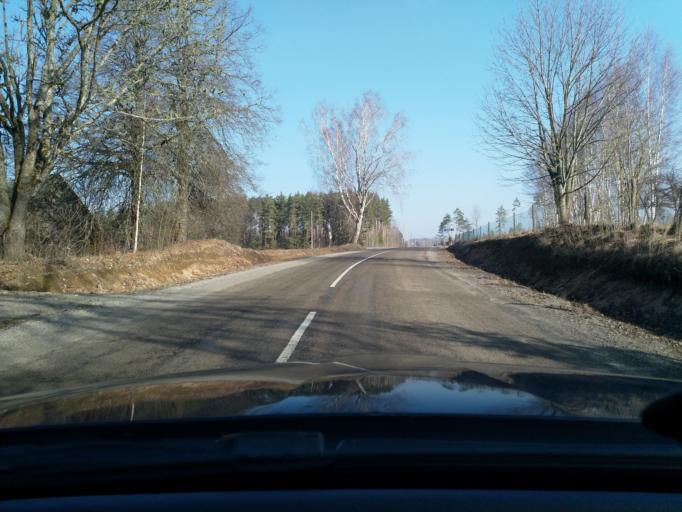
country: LV
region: Kuldigas Rajons
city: Kuldiga
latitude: 56.8700
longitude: 21.9400
